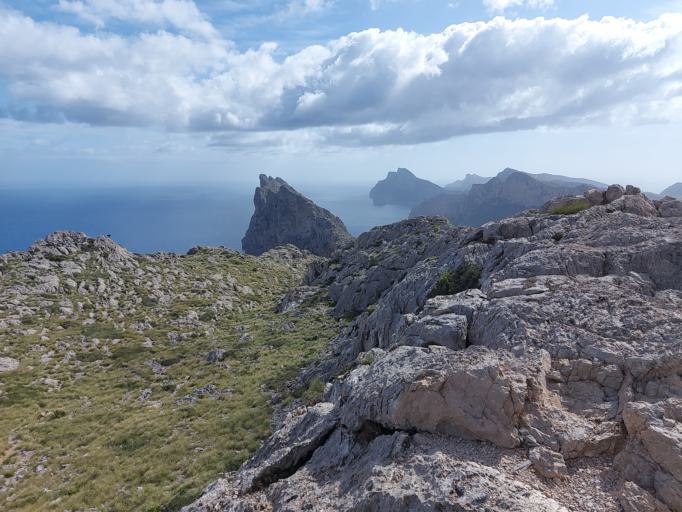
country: ES
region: Balearic Islands
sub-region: Illes Balears
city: Pollenca
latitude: 39.9187
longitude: 3.0733
